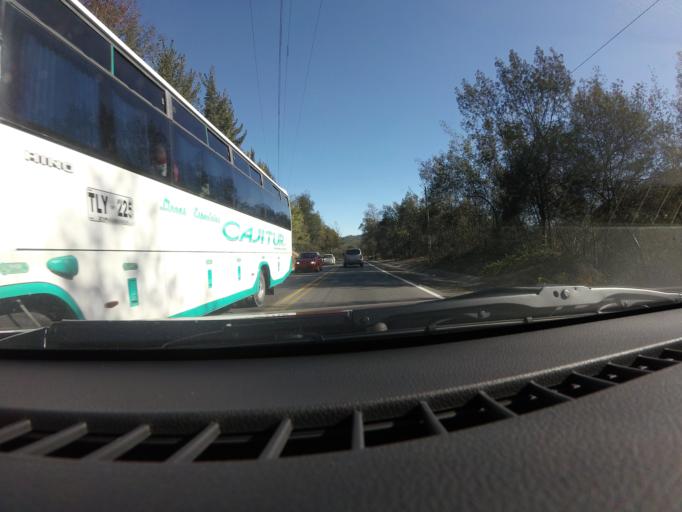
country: CO
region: Cundinamarca
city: Sutatausa
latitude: 5.2314
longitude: -73.8563
